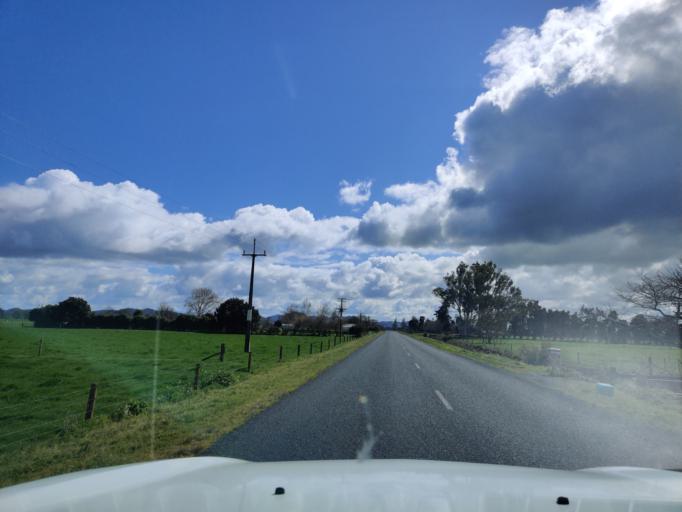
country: NZ
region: Waikato
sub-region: Waikato District
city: Ngaruawahia
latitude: -37.6046
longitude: 175.3040
